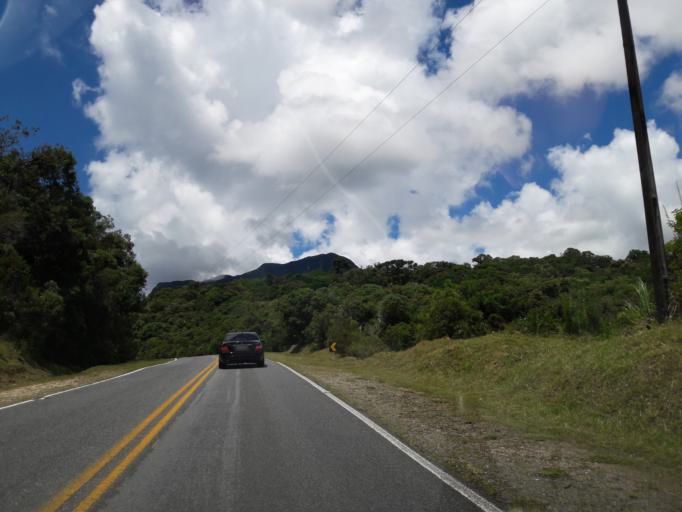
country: BR
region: Parana
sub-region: Campina Grande Do Sul
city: Campina Grande do Sul
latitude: -25.3239
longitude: -48.9214
